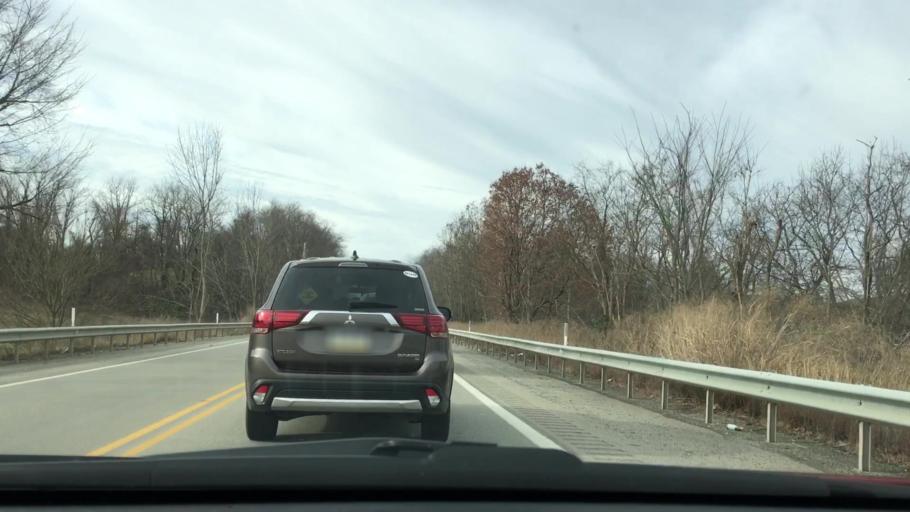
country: US
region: Pennsylvania
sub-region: Fayette County
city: Masontown
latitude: 39.8927
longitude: -79.8317
